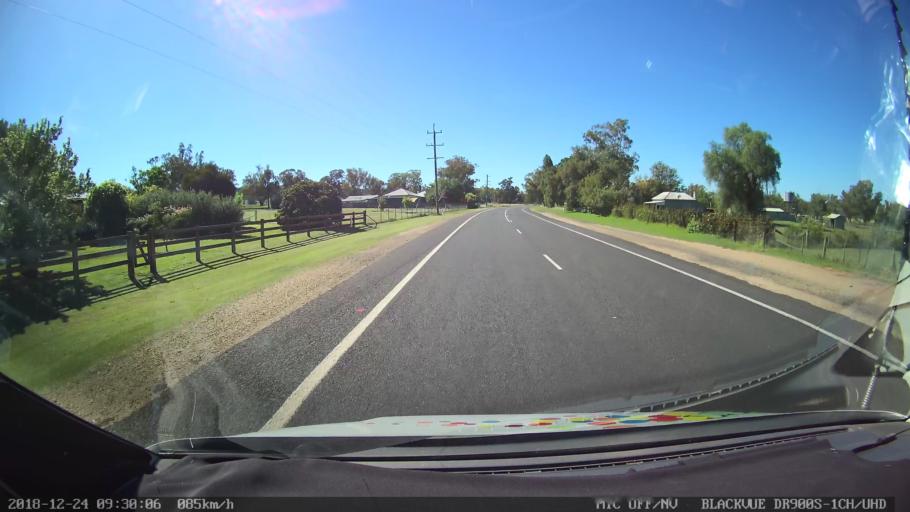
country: AU
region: New South Wales
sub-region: Liverpool Plains
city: Quirindi
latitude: -31.5583
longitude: 150.6960
